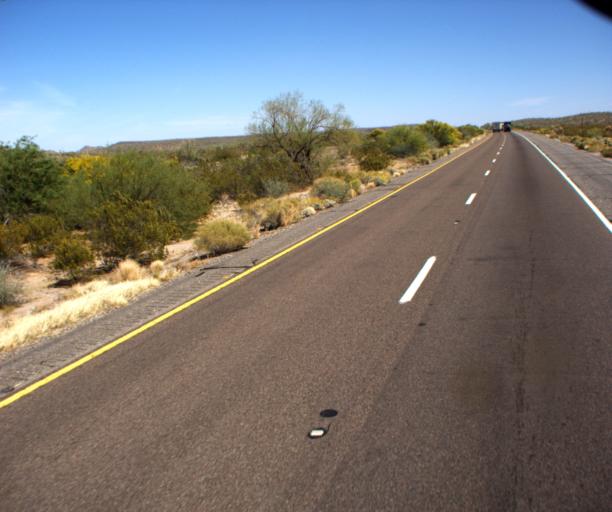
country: US
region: Arizona
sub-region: Pinal County
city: Maricopa
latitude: 32.8504
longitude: -112.3542
